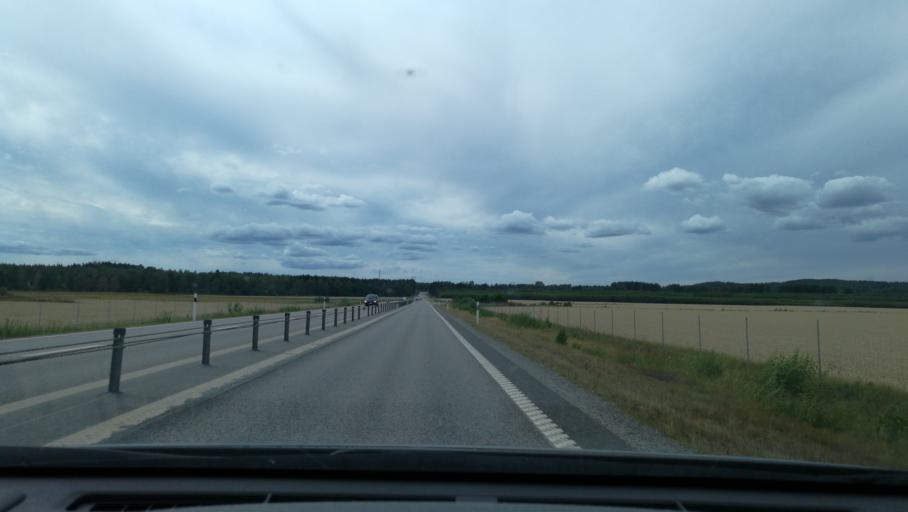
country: SE
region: OEstergoetland
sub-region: Norrkopings Kommun
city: Jursla
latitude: 58.6331
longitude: 16.1311
